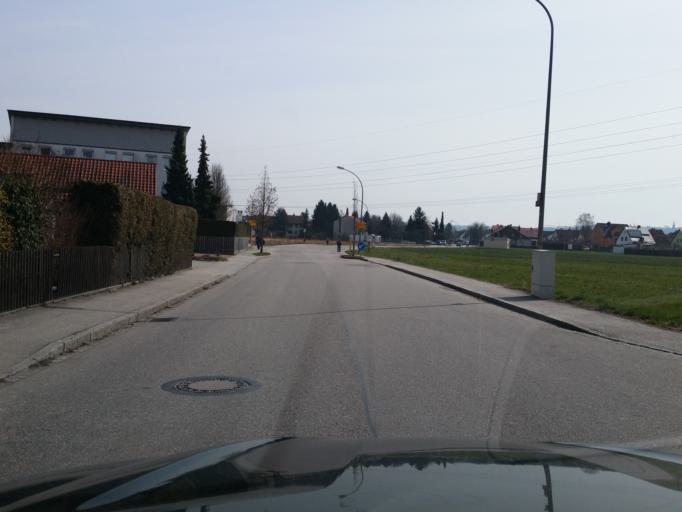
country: DE
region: Bavaria
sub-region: Lower Bavaria
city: Landshut
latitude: 48.5547
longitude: 12.1172
